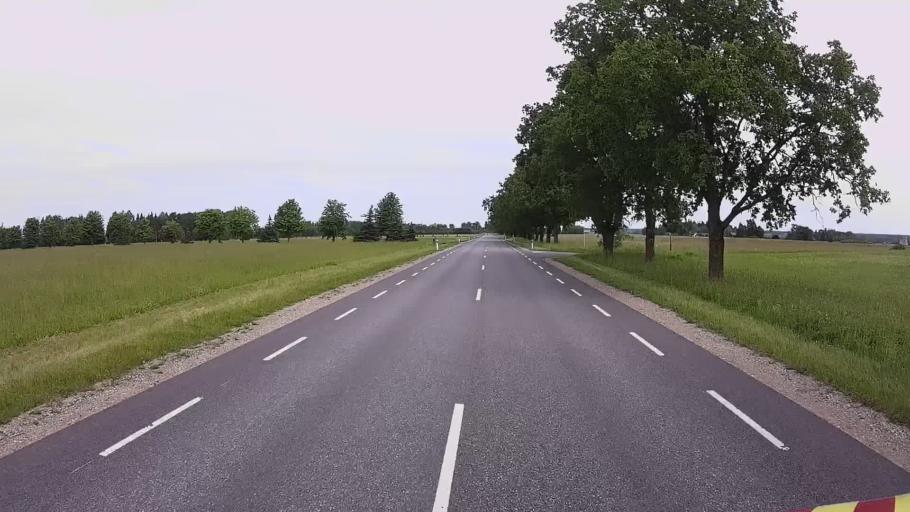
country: EE
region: Viljandimaa
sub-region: Karksi vald
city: Karksi-Nuia
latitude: 58.1247
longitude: 25.5826
